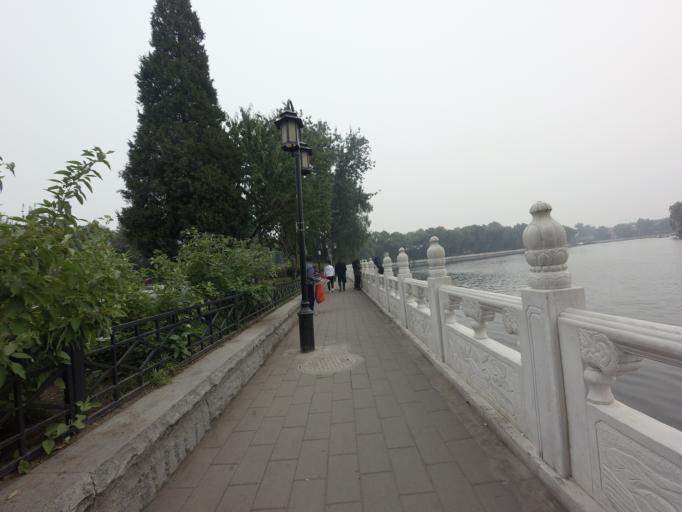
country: CN
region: Beijing
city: Jingshan
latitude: 39.9359
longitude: 116.3887
